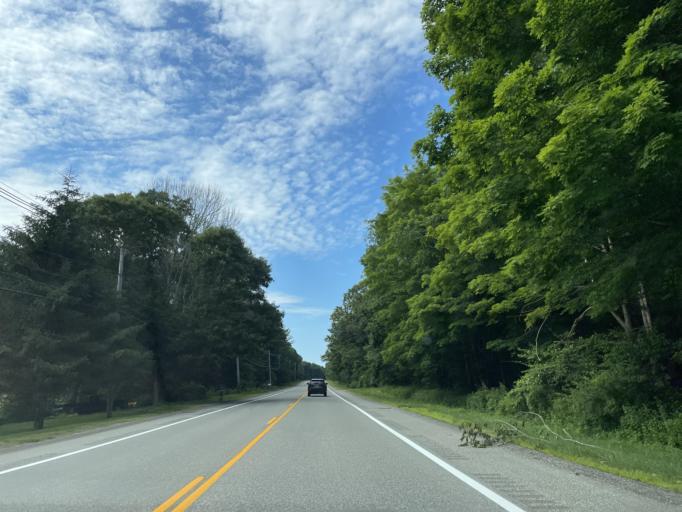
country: US
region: Rhode Island
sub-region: Kent County
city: West Greenwich
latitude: 41.6515
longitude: -71.6935
